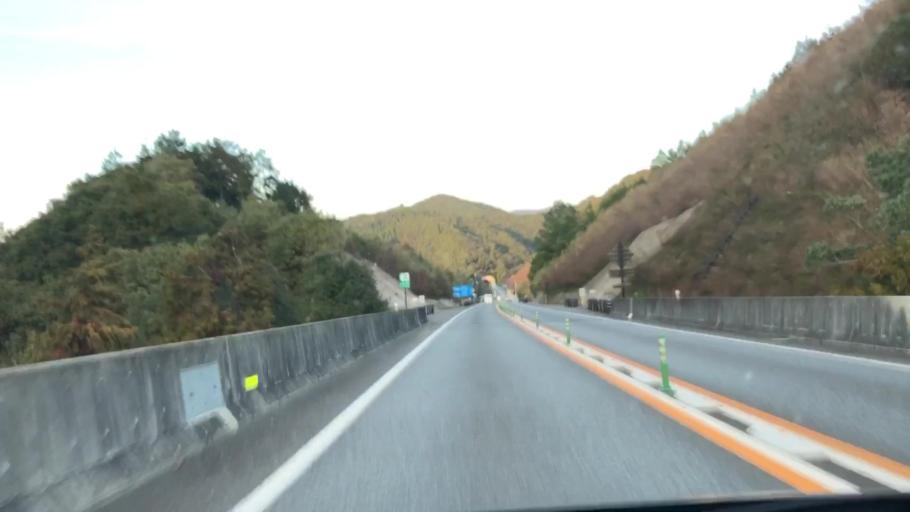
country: JP
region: Kumamoto
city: Minamata
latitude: 32.2768
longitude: 130.4960
